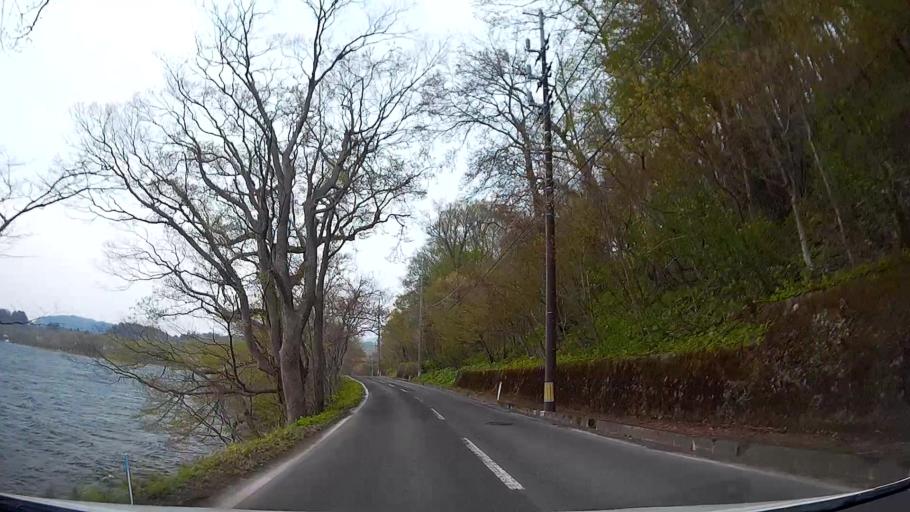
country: JP
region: Akita
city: Hanawa
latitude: 40.4192
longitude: 140.8907
